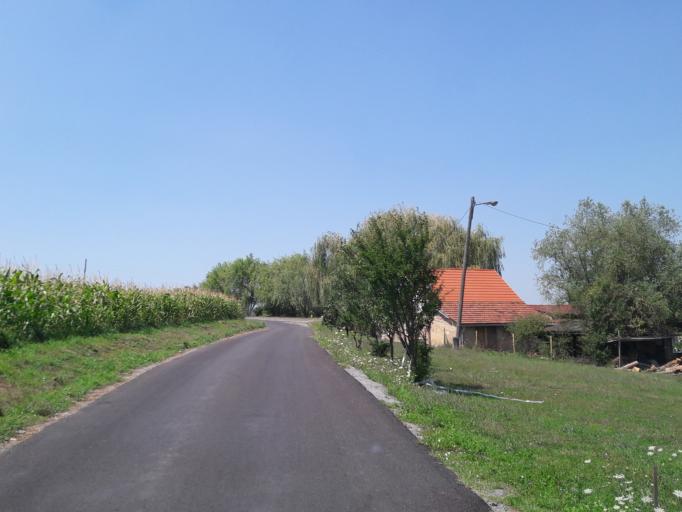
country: HR
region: Osjecko-Baranjska
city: Viskovci
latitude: 45.3379
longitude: 18.4235
